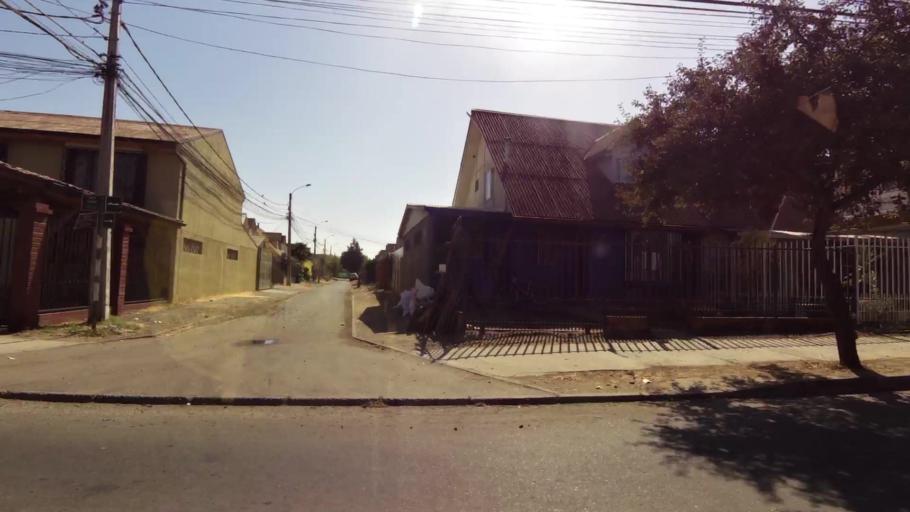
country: CL
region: Maule
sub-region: Provincia de Talca
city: Talca
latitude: -35.4080
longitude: -71.6440
